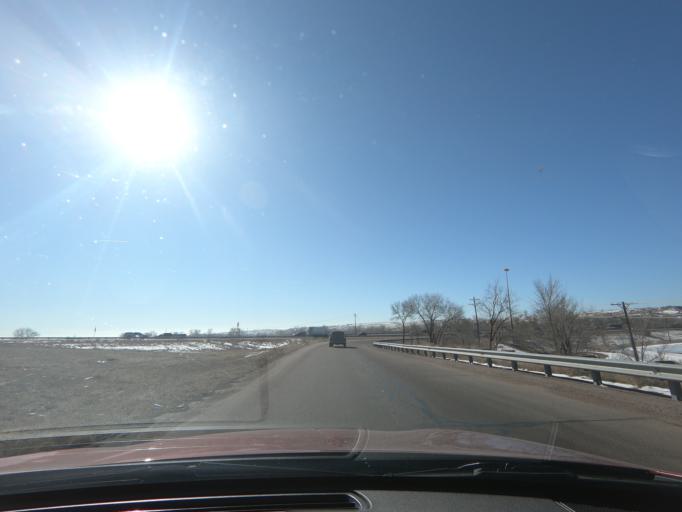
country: US
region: Colorado
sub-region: El Paso County
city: Stratmoor
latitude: 38.7676
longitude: -104.7634
